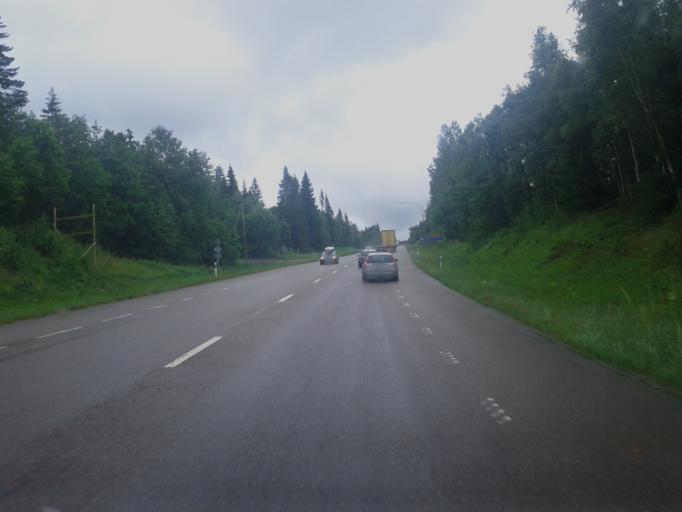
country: SE
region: Vaesternorrland
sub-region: Haernoesands Kommun
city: Haernoesand
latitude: 62.6953
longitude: 17.8527
